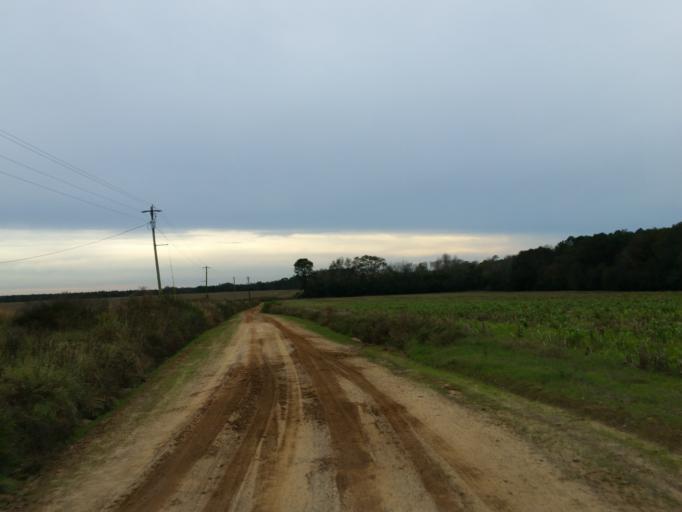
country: US
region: Georgia
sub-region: Crisp County
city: Cordele
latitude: 31.8933
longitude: -83.7168
